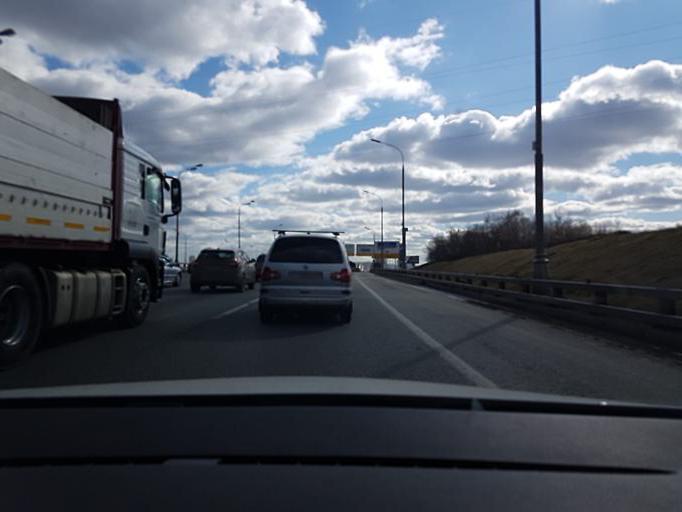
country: RU
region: Moscow
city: Strogino
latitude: 55.8369
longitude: 37.3956
